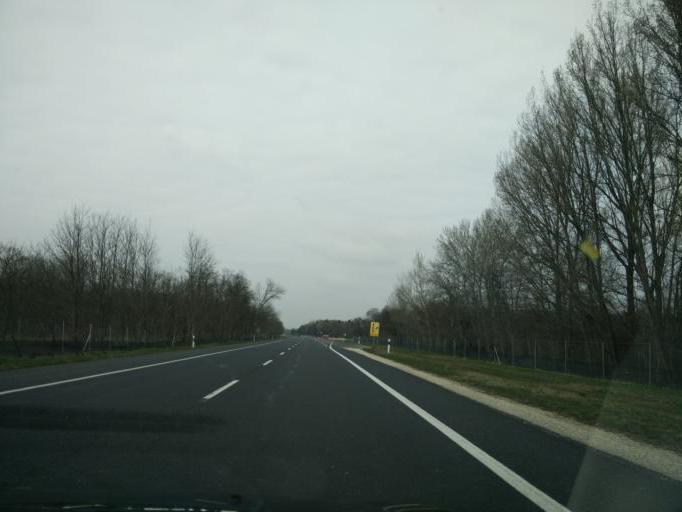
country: HU
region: Gyor-Moson-Sopron
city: Toltestava
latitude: 47.7087
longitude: 17.7511
